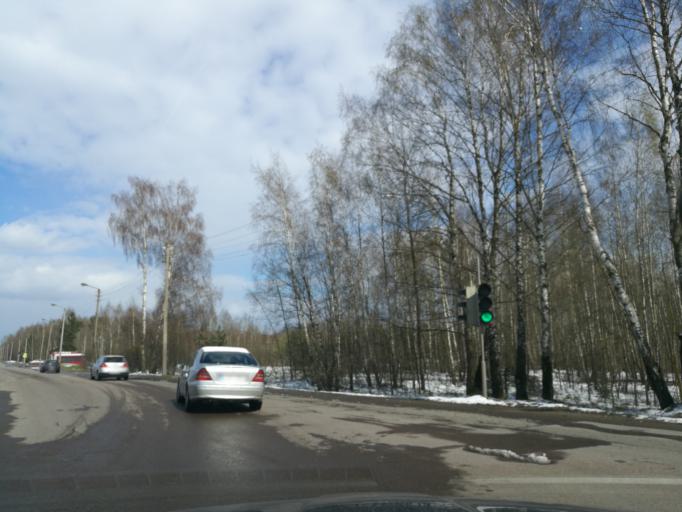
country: LT
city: Ramuciai
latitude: 54.9177
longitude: 24.0406
